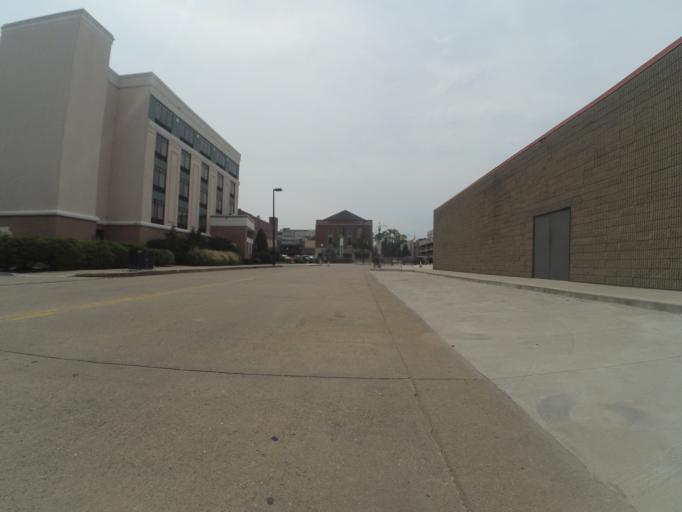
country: US
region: West Virginia
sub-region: Cabell County
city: Huntington
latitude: 38.4224
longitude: -82.4459
